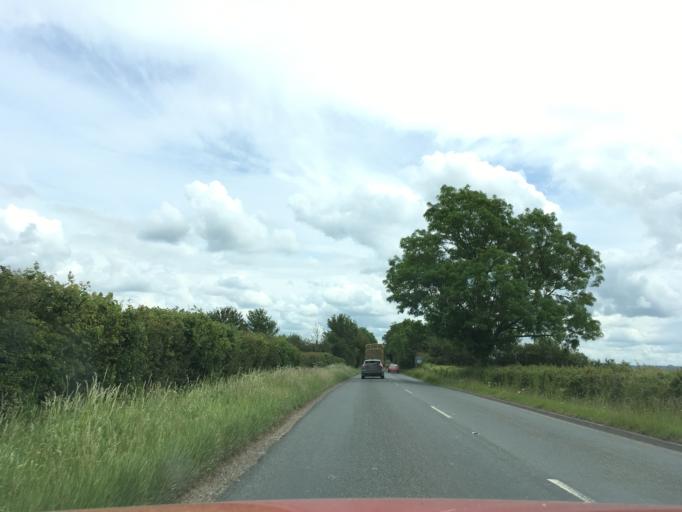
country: GB
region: England
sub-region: Wiltshire
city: Royal Wootton Bassett
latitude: 51.5622
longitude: -1.9436
